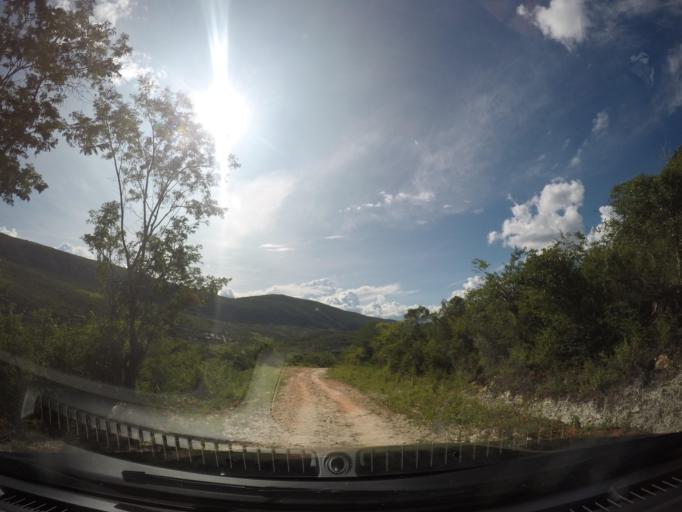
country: BR
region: Bahia
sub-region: Livramento Do Brumado
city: Livramento do Brumado
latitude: -13.2156
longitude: -41.6032
